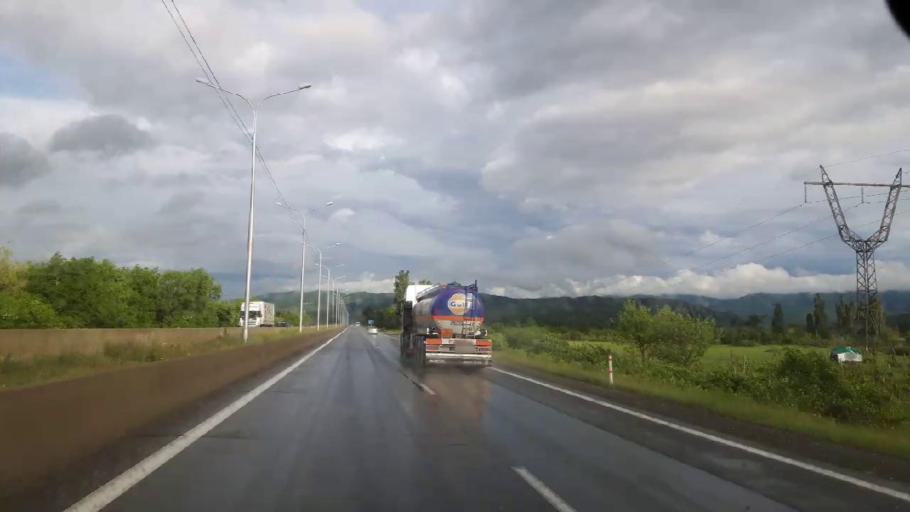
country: GE
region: Shida Kartli
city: Kaspi
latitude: 41.9219
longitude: 44.5456
